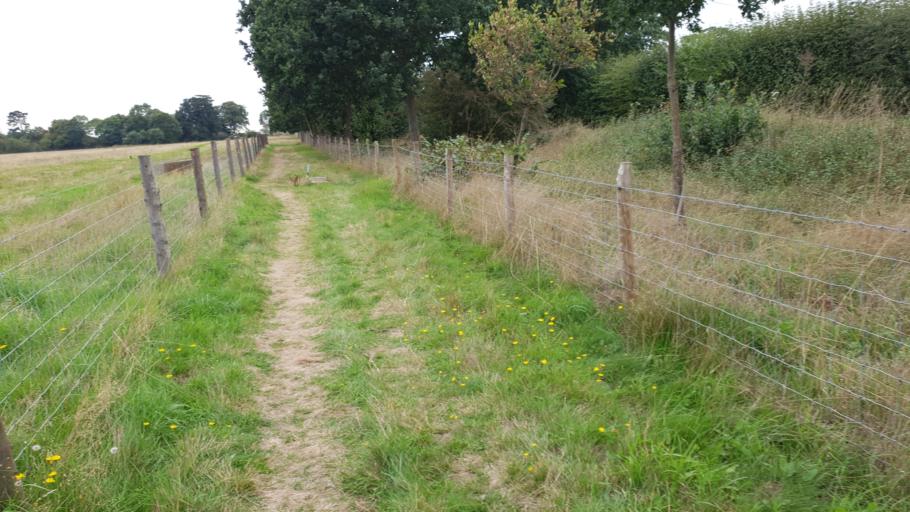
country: GB
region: England
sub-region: Essex
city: Manningtree
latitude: 51.9436
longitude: 1.0360
